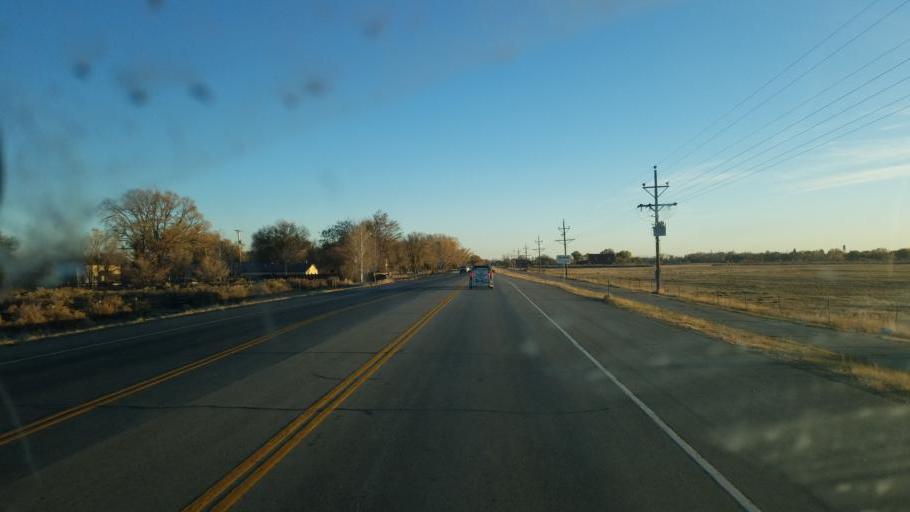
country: US
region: Colorado
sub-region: Alamosa County
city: Alamosa East
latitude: 37.4867
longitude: -105.8574
